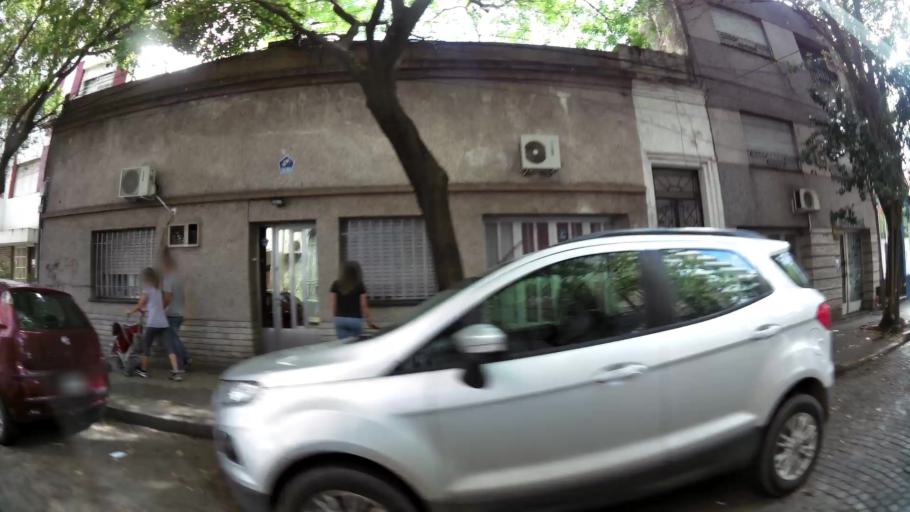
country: AR
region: Santa Fe
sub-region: Departamento de Rosario
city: Rosario
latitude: -32.9559
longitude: -60.6358
